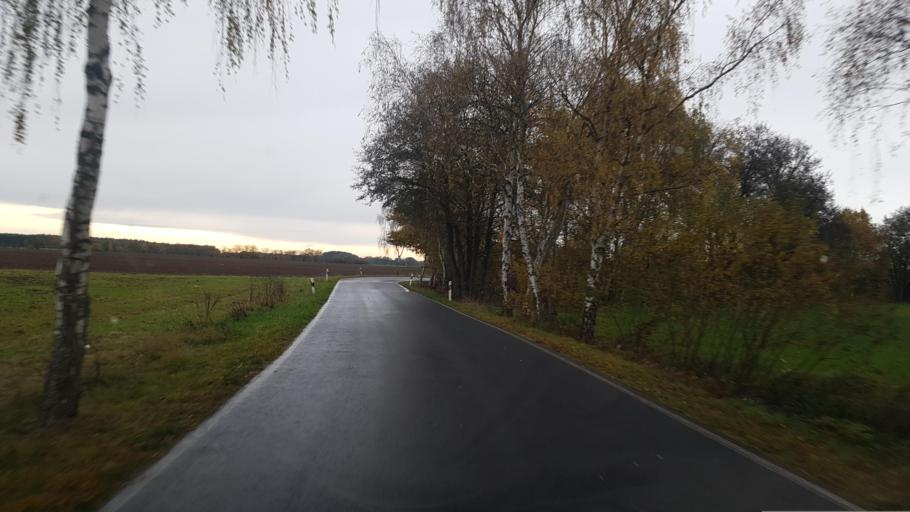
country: DE
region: Saxony-Anhalt
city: Abtsdorf
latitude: 51.8743
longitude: 12.7443
